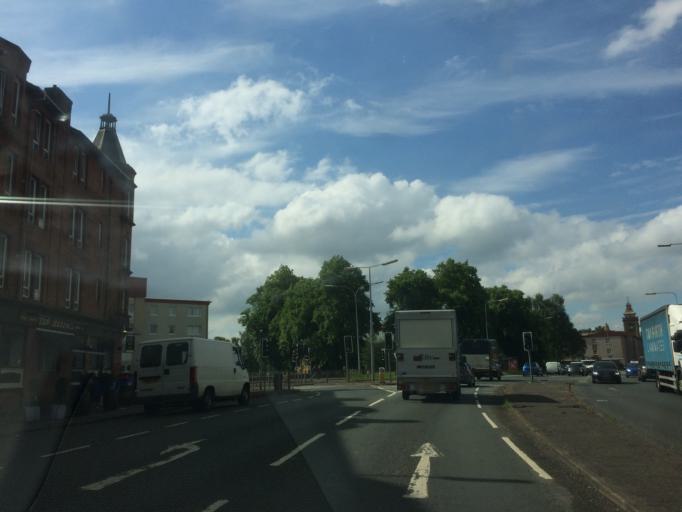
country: GB
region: Scotland
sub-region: East Renfrewshire
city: Giffnock
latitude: 55.8279
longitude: -4.2959
